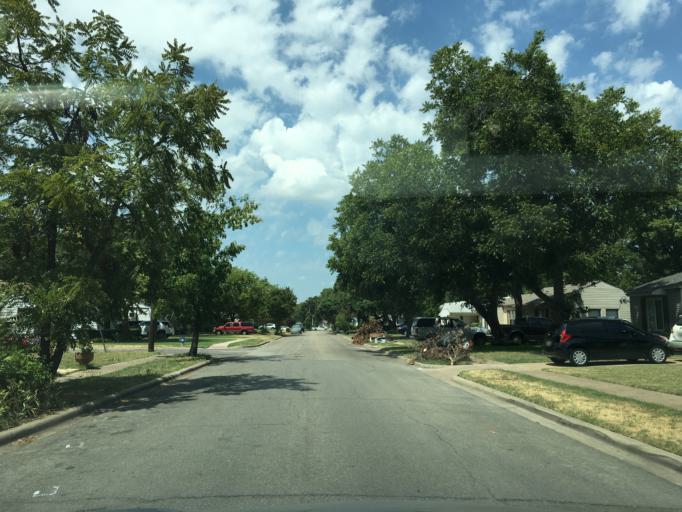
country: US
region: Texas
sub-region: Dallas County
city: Garland
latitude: 32.8591
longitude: -96.6796
